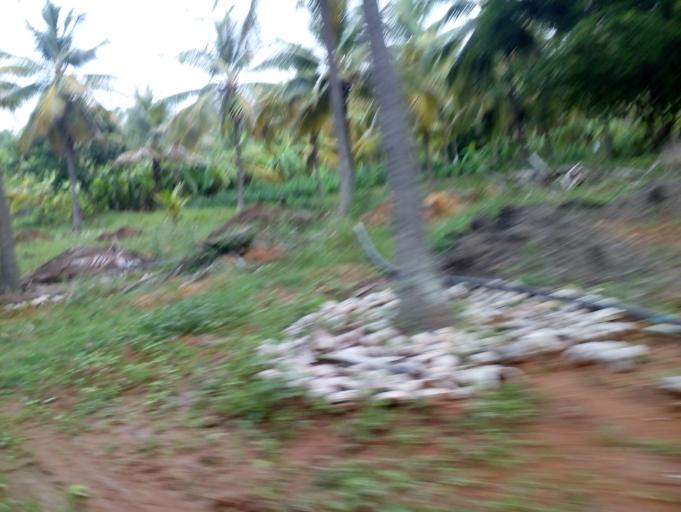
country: IN
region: Karnataka
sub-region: Tumkur
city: Turuvekere
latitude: 13.1911
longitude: 76.7176
